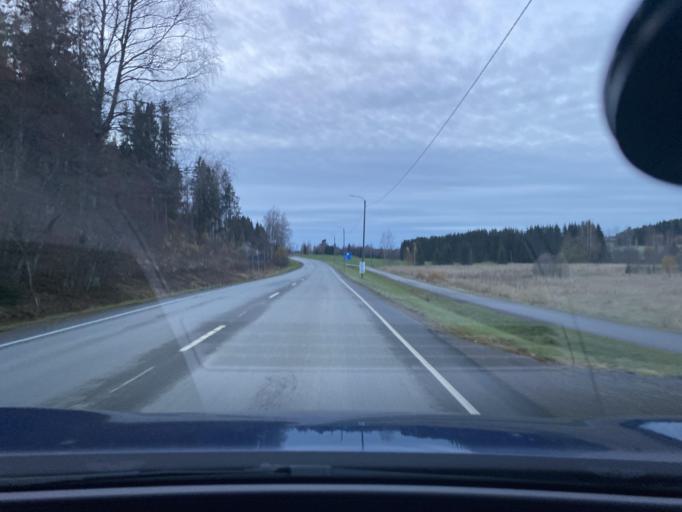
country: FI
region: Uusimaa
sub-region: Helsinki
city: Saukkola
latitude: 60.3810
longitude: 23.9536
